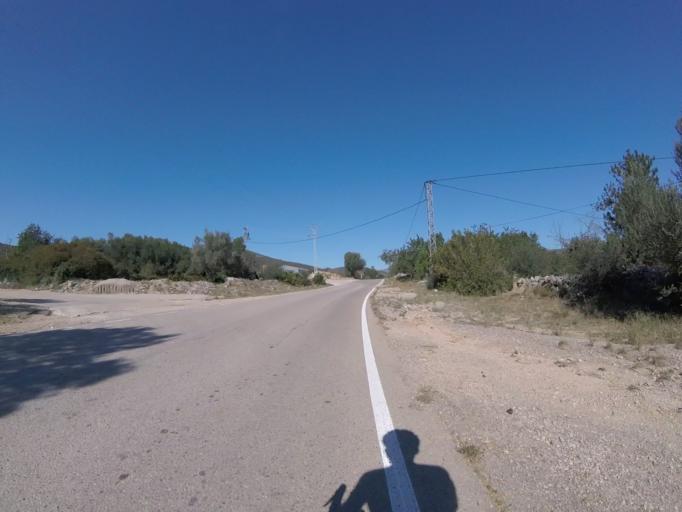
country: ES
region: Valencia
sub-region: Provincia de Castello
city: Santa Magdalena de Pulpis
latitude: 40.3615
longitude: 0.2825
